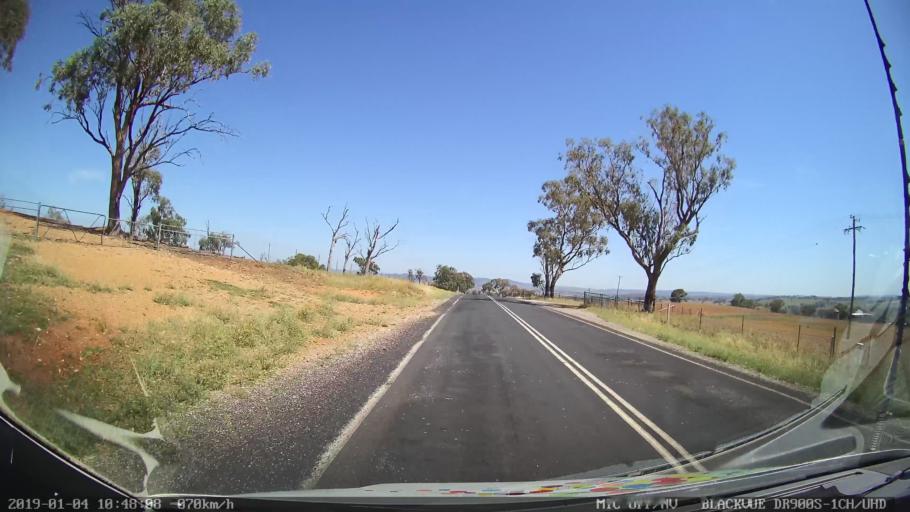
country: AU
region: New South Wales
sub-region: Cabonne
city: Molong
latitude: -33.2631
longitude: 148.7149
